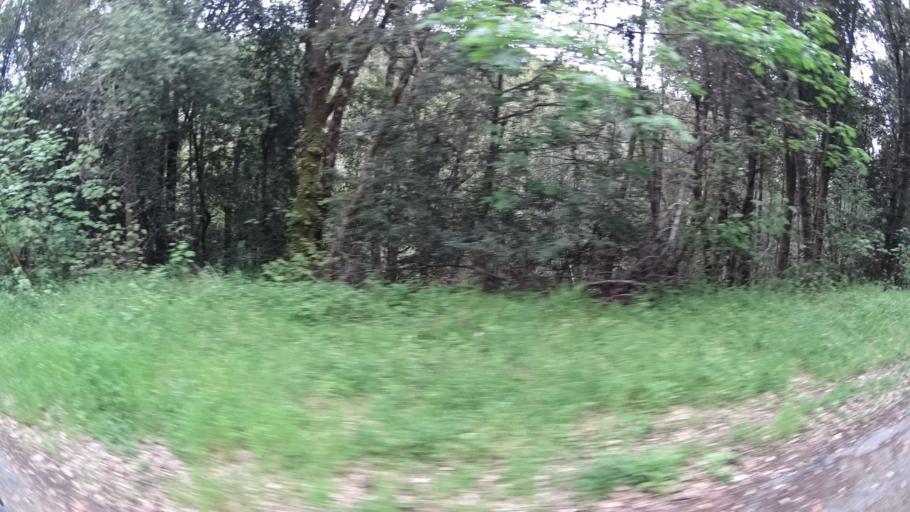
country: US
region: California
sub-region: Humboldt County
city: Blue Lake
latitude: 40.9526
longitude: -123.8386
